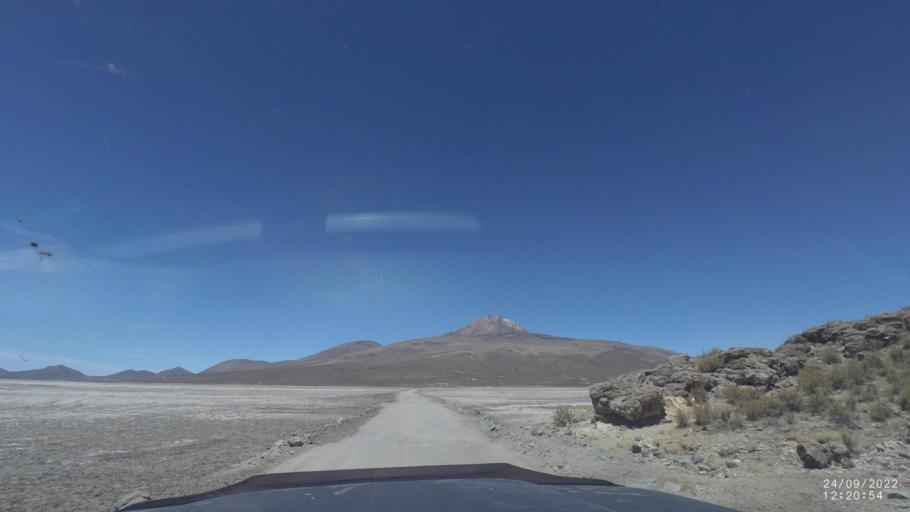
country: BO
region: Potosi
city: Colchani
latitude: -19.7457
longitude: -67.6704
